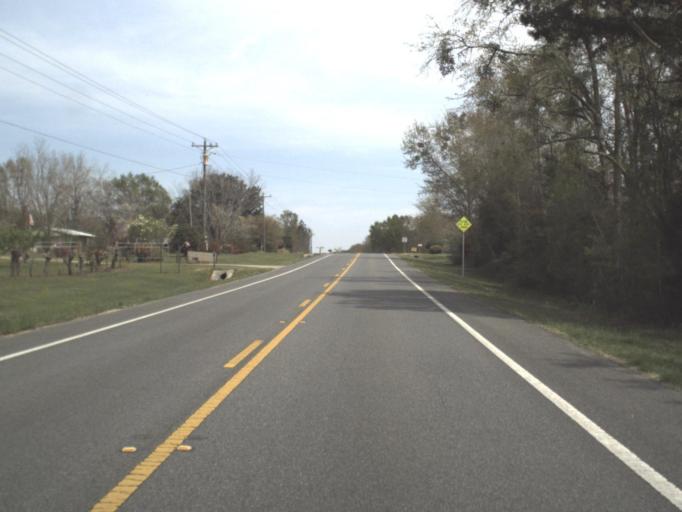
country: US
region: Alabama
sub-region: Geneva County
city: Geneva
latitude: 30.9527
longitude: -85.9203
